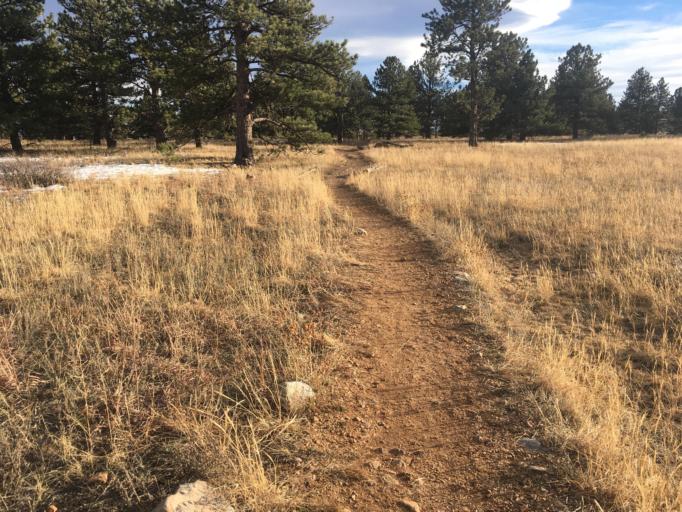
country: US
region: Colorado
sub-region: Boulder County
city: Superior
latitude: 39.9174
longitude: -105.2487
